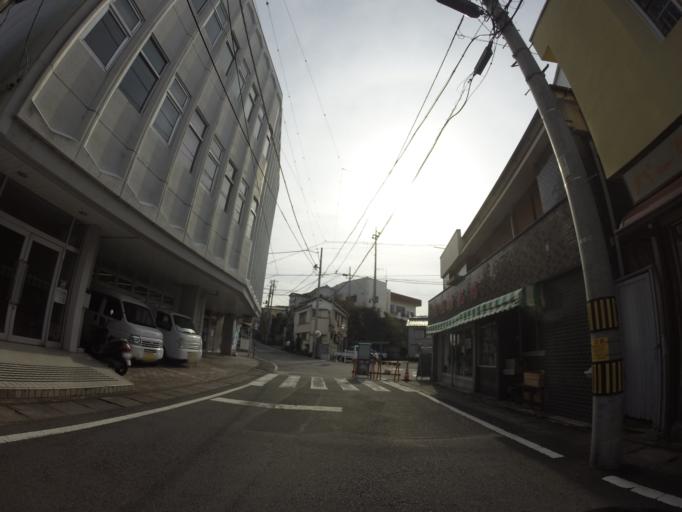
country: JP
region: Shizuoka
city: Heda
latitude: 34.8036
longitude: 138.7638
